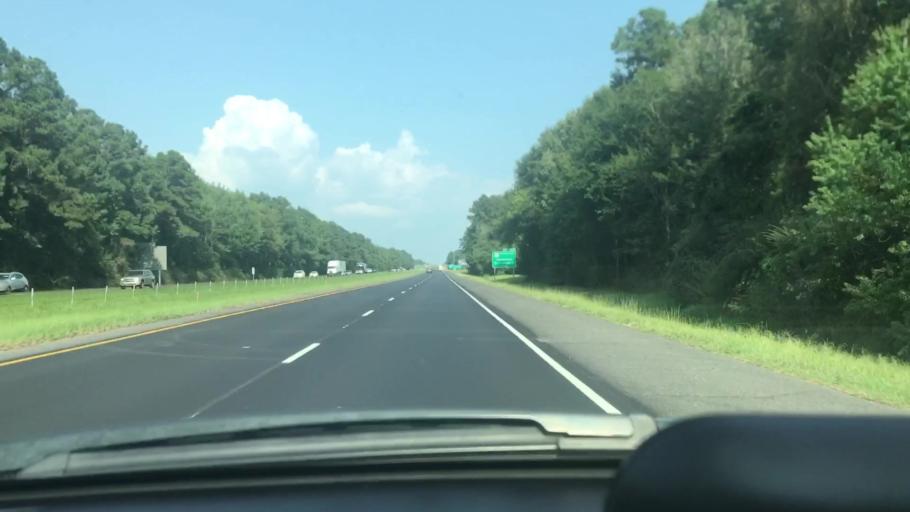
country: US
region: Louisiana
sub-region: Tangipahoa Parish
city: Hammond
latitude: 30.4789
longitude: -90.4787
